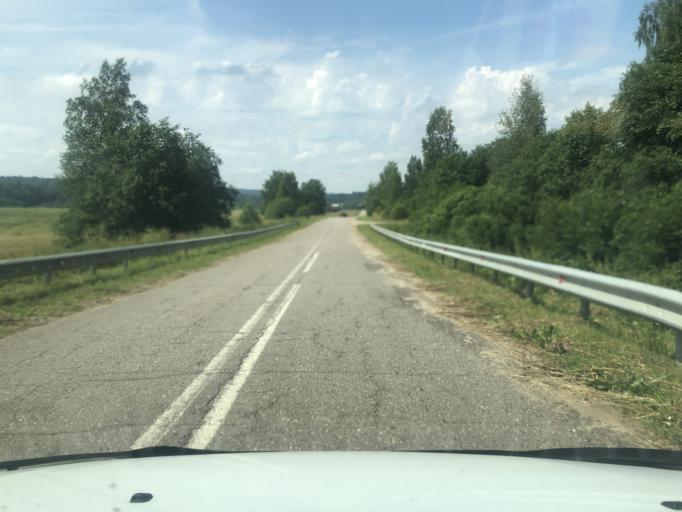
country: RU
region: Jaroslavl
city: Pereslavl'-Zalesskiy
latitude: 57.0406
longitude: 38.8747
